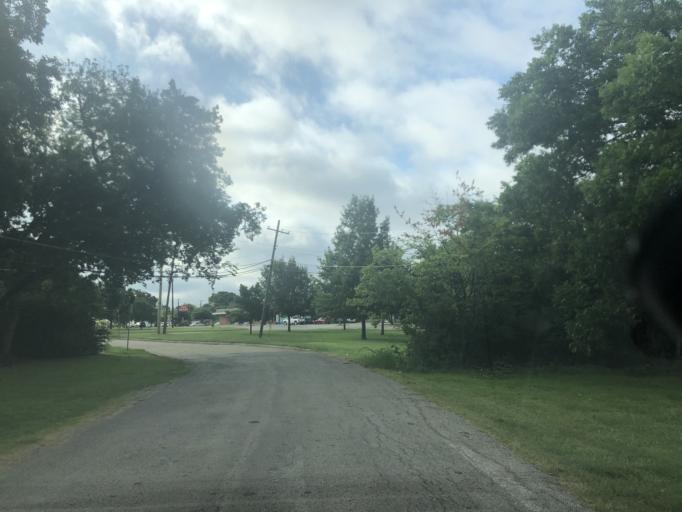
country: US
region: Texas
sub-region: Dallas County
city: University Park
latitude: 32.8518
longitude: -96.8406
